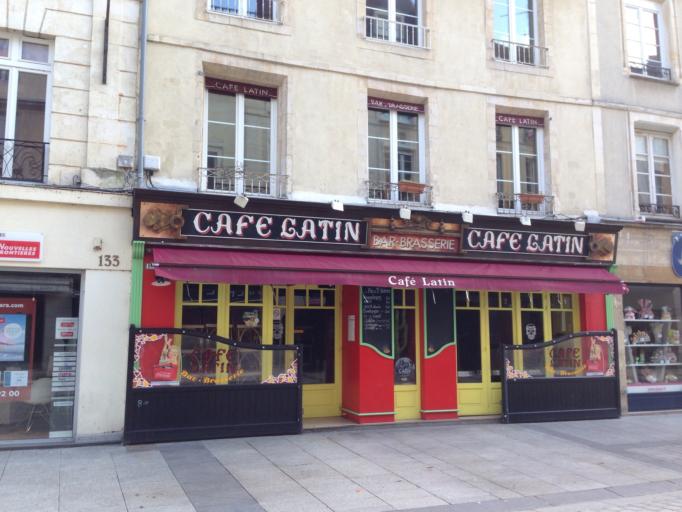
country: FR
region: Lower Normandy
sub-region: Departement du Calvados
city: Caen
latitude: 49.1822
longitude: -0.3659
